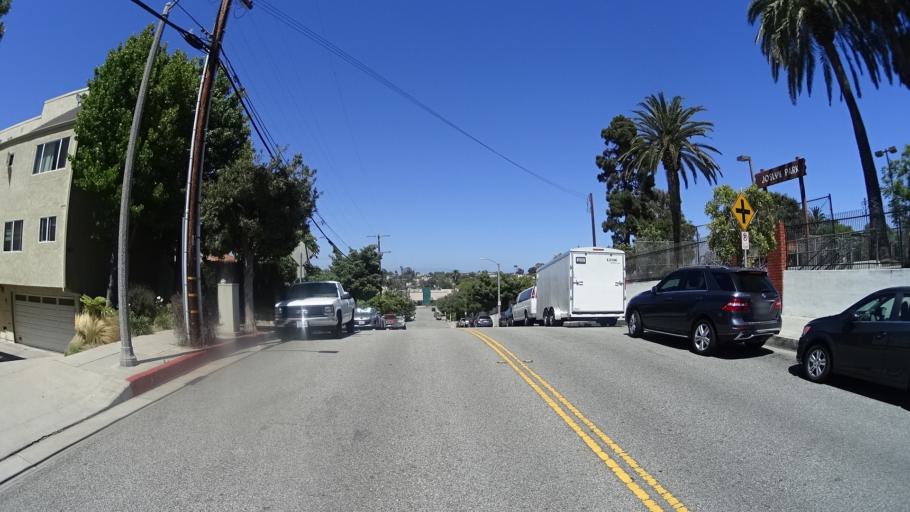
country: US
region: California
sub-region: Los Angeles County
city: Santa Monica
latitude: 34.0086
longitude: -118.4819
